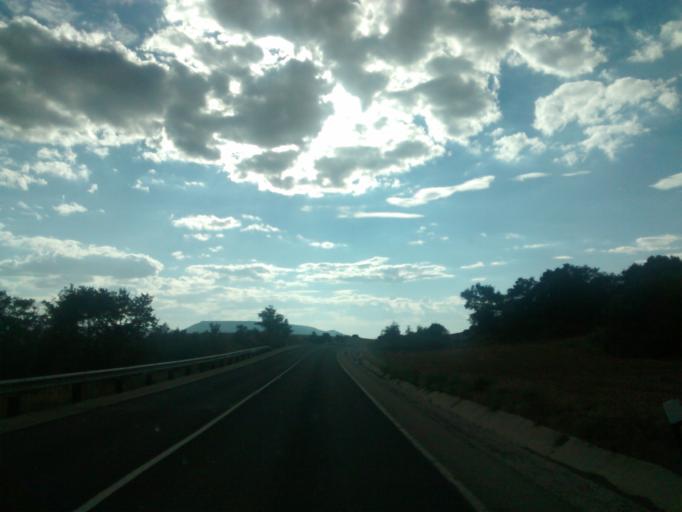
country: ES
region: Castille and Leon
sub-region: Provincia de Burgos
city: Basconcillos del Tozo
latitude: 42.6836
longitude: -3.9611
